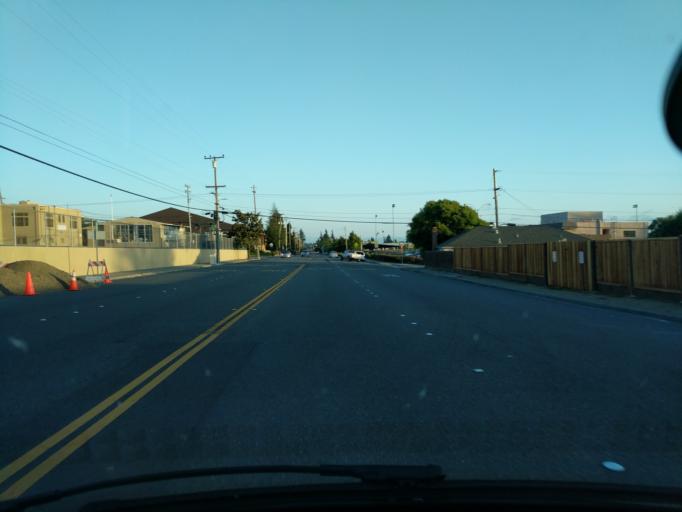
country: US
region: California
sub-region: Alameda County
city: Castro Valley
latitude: 37.7078
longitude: -122.0740
